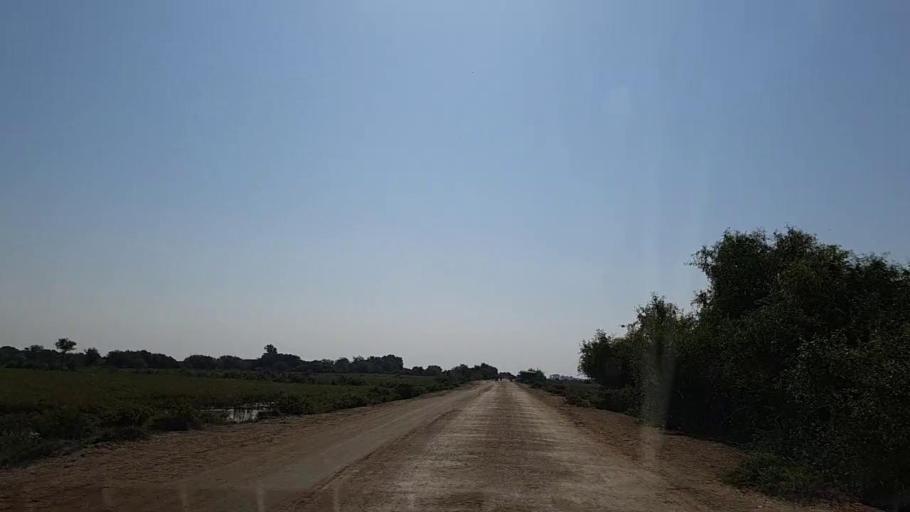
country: PK
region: Sindh
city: Chuhar Jamali
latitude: 24.5174
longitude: 68.0947
